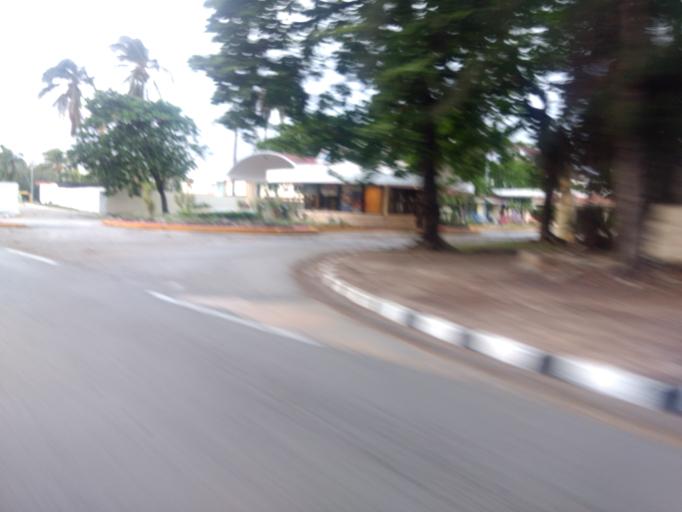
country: CU
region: La Habana
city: Cerro
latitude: 23.0887
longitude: -82.4761
